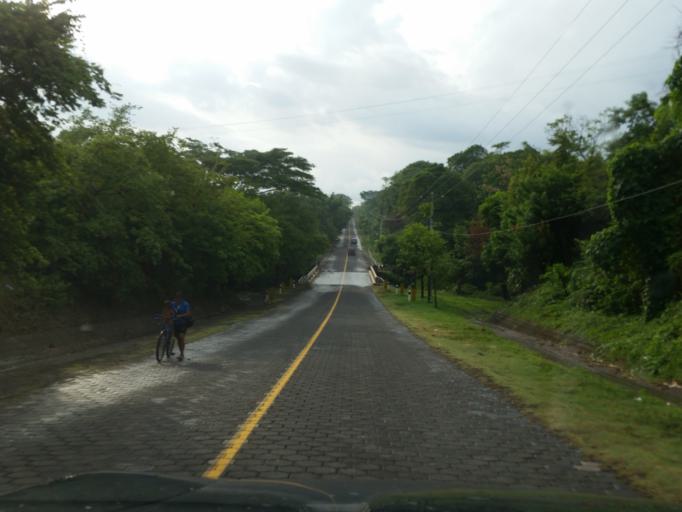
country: NI
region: Managua
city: Masachapa
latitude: 11.8258
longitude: -86.5010
